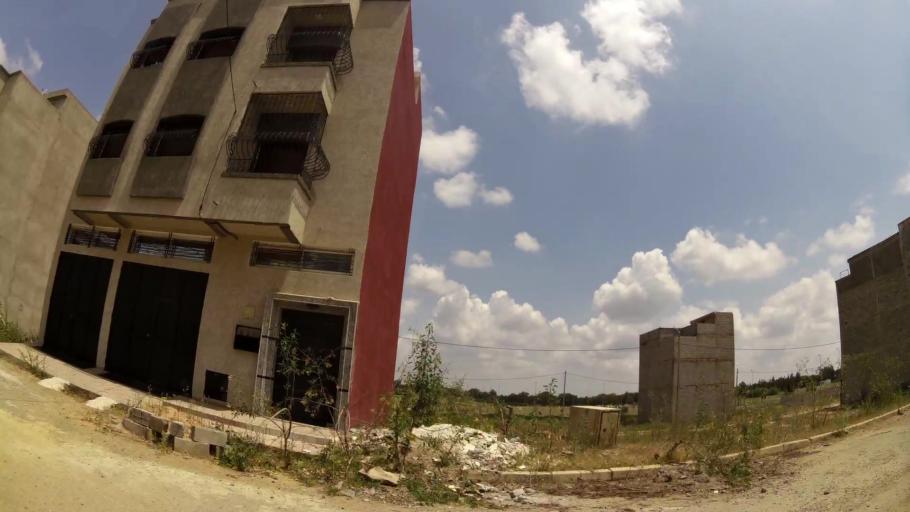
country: MA
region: Rabat-Sale-Zemmour-Zaer
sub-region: Khemisset
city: Tiflet
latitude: 34.0127
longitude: -6.5204
